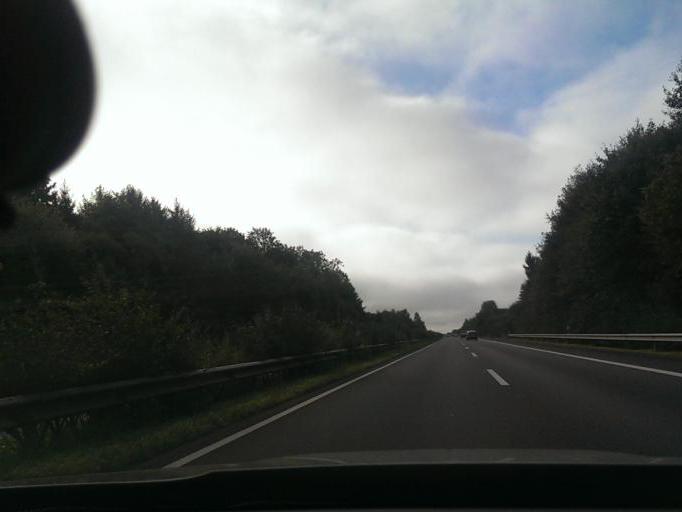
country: DE
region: Lower Saxony
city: Flothe
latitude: 52.1047
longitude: 10.4900
